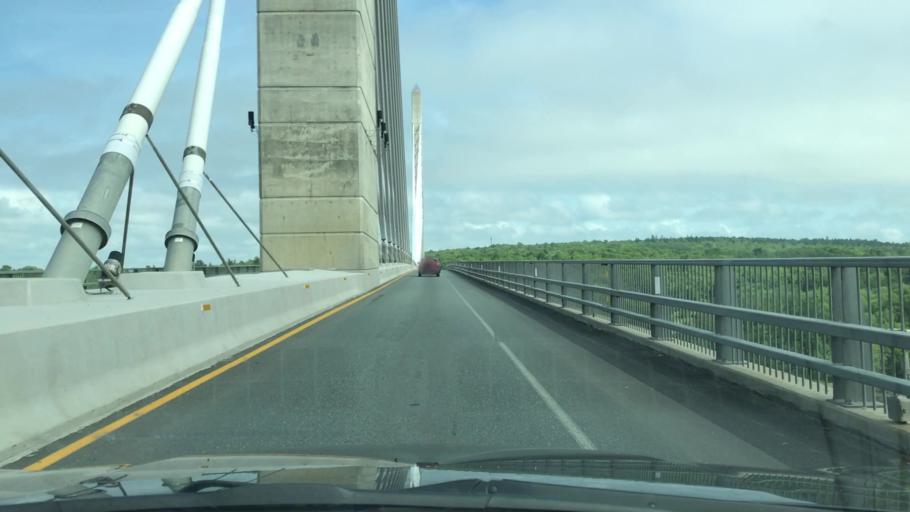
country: US
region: Maine
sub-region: Hancock County
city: Bucksport
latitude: 44.5606
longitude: -68.8042
